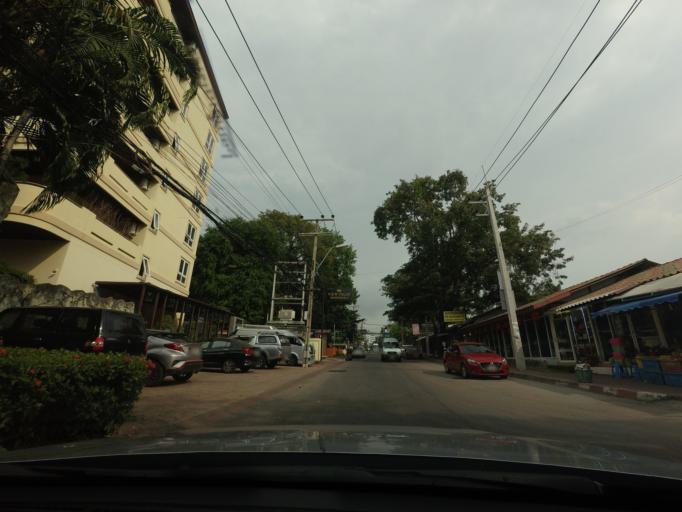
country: TH
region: Chon Buri
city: Phatthaya
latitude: 12.9570
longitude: 100.8871
